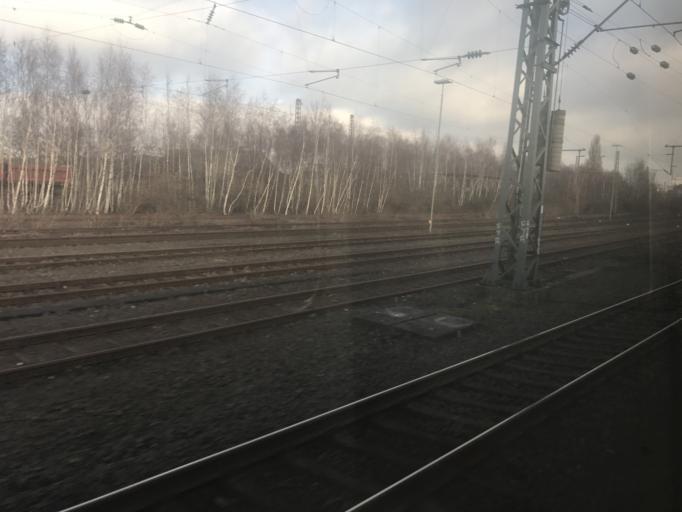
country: DE
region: North Rhine-Westphalia
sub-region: Regierungsbezirk Arnsberg
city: Bochum
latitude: 51.4710
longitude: 7.2063
